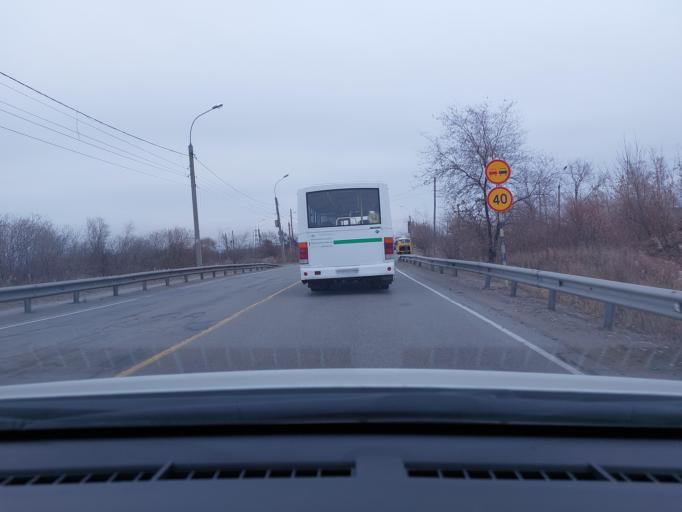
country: RU
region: Irkutsk
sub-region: Irkutskiy Rayon
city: Irkutsk
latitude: 52.3311
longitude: 104.2299
